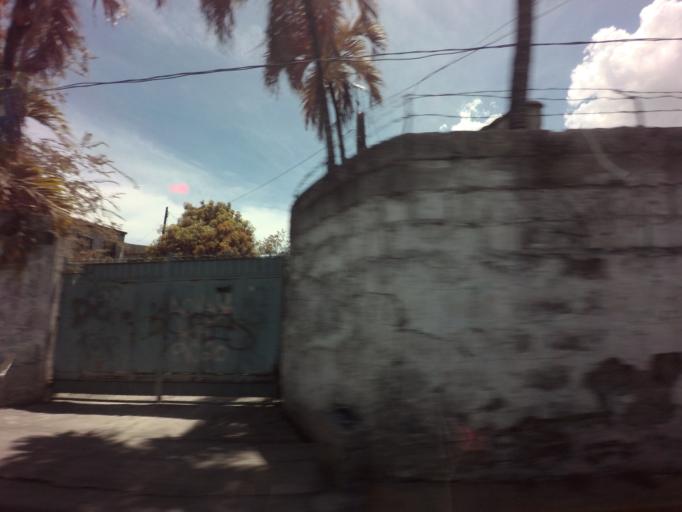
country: PH
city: Sambayanihan People's Village
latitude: 14.4906
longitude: 120.9885
